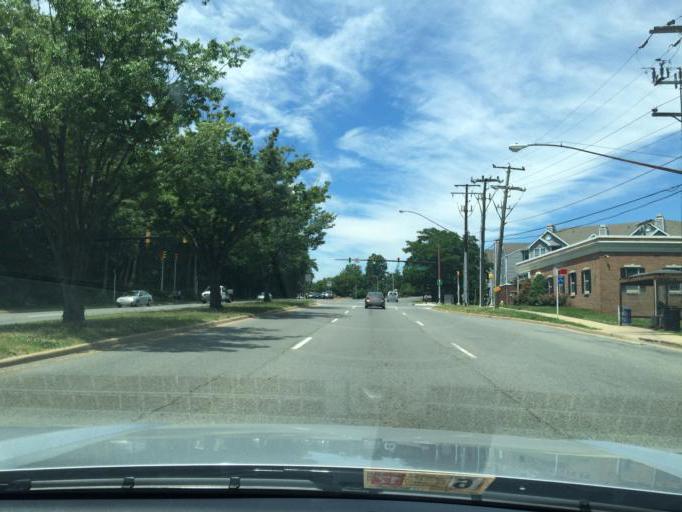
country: US
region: Virginia
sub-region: Fairfax County
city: Lincolnia
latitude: 38.8132
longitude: -77.1257
